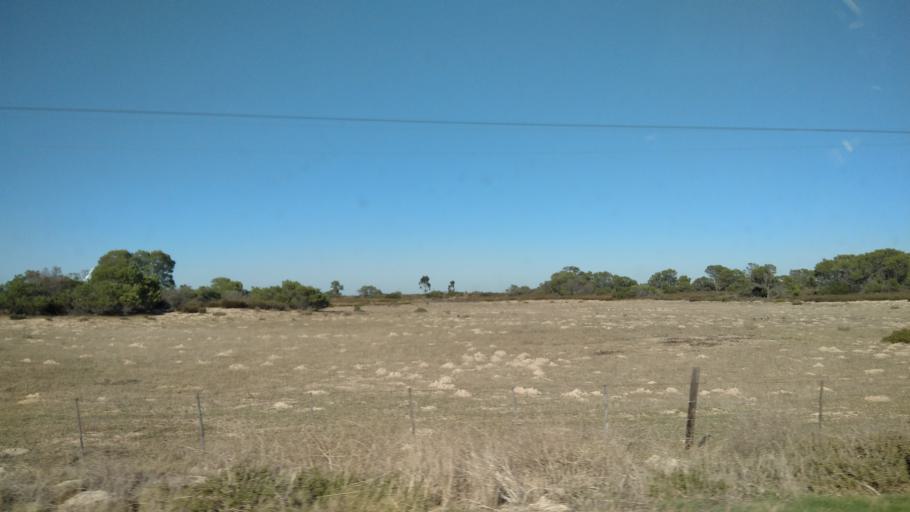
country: ZA
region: Western Cape
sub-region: West Coast District Municipality
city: Moorreesburg
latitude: -33.0709
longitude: 18.3723
